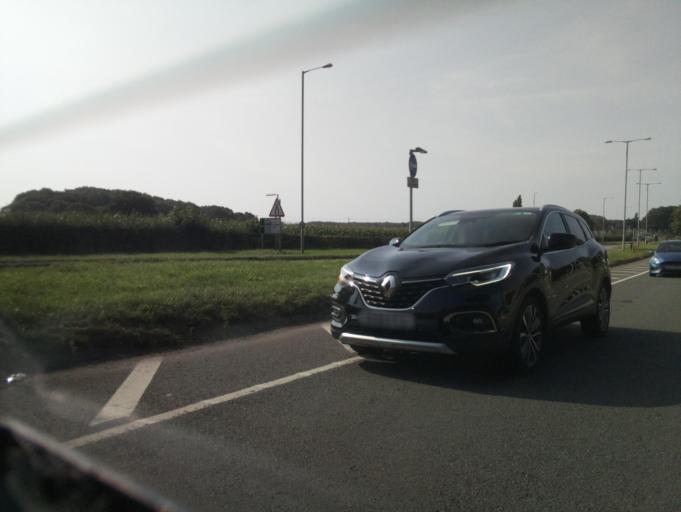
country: GB
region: England
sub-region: Walsall
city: Brownhills
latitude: 52.6437
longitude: -1.9040
